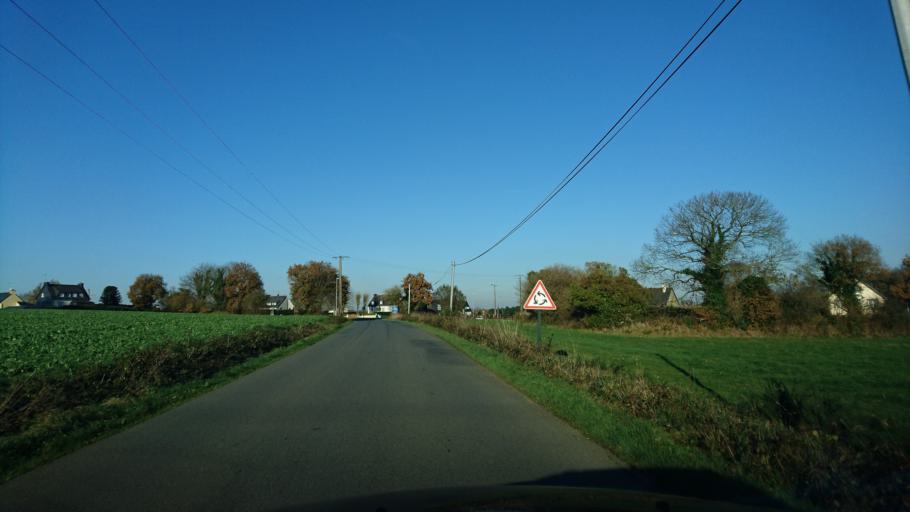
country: FR
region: Brittany
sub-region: Departement des Cotes-d'Armor
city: Pedernec
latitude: 48.5897
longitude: -3.2613
